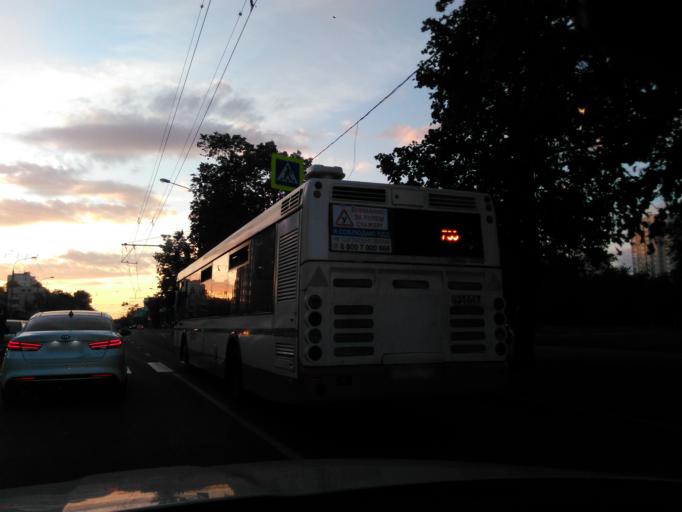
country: RU
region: Moscow
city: Zapadnoye Degunino
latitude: 55.8766
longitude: 37.5241
